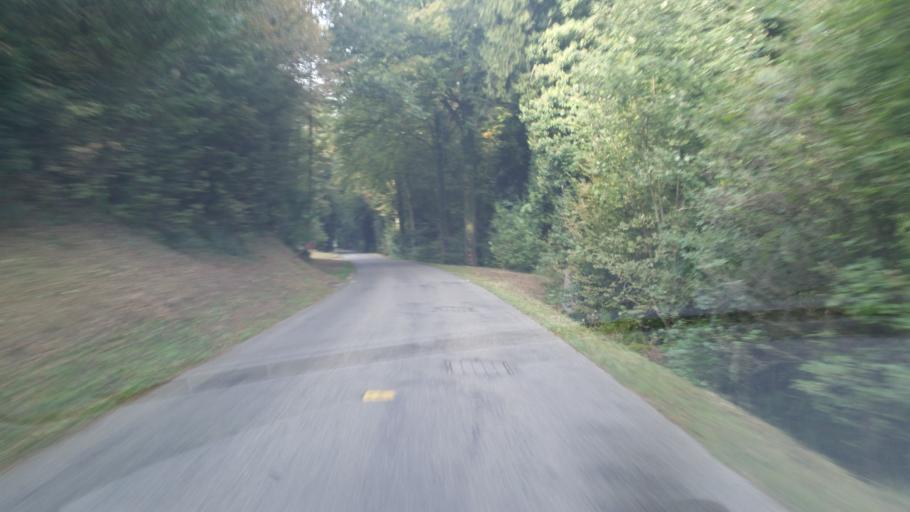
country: CH
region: Aargau
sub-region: Bezirk Baden
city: Mellingen
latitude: 47.3960
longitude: 8.2802
